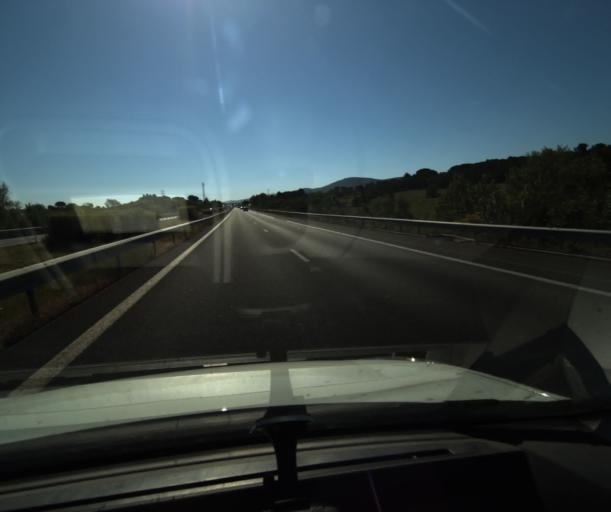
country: FR
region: Languedoc-Roussillon
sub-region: Departement de l'Aude
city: Trebes
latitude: 43.1958
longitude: 2.4370
